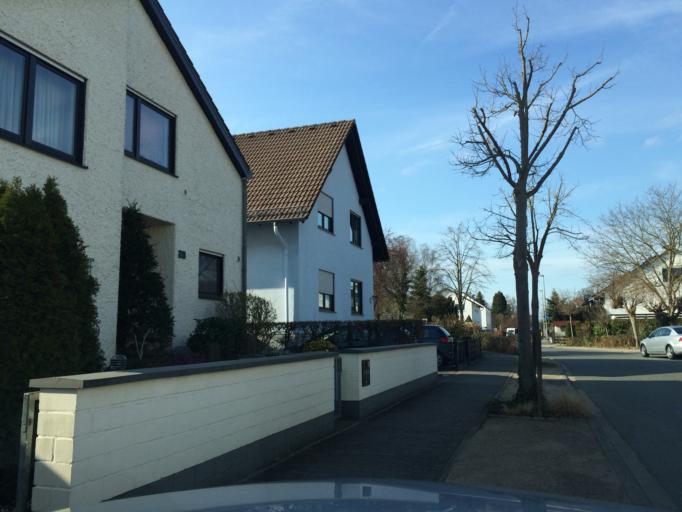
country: DE
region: Hesse
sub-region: Regierungsbezirk Darmstadt
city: Nauheim
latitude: 49.9551
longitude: 8.4621
